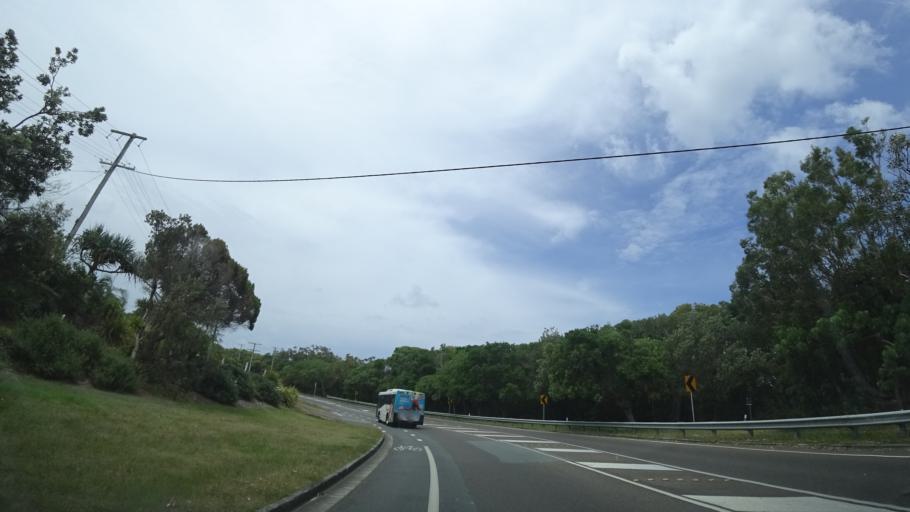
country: AU
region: Queensland
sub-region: Sunshine Coast
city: Coolum Beach
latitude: -26.5493
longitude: 153.1001
